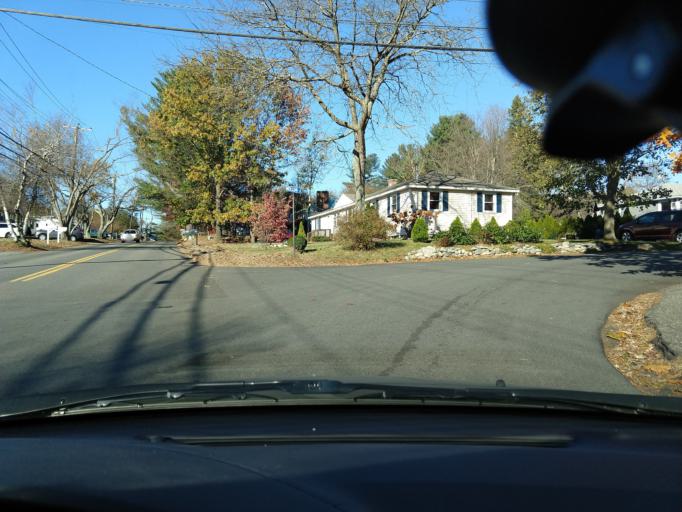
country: US
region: Massachusetts
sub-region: Middlesex County
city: Bedford
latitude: 42.4741
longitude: -71.2663
